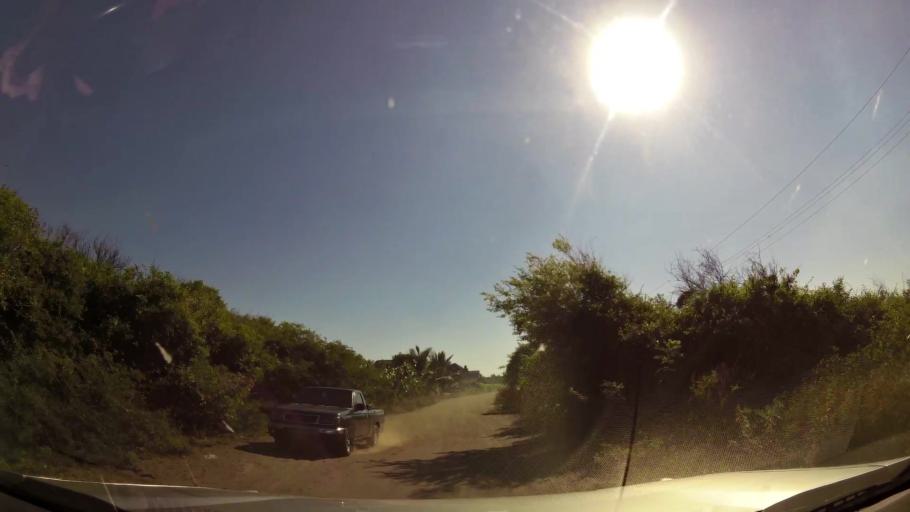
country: GT
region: Jutiapa
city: Pasaco
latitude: 13.8526
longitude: -90.3804
